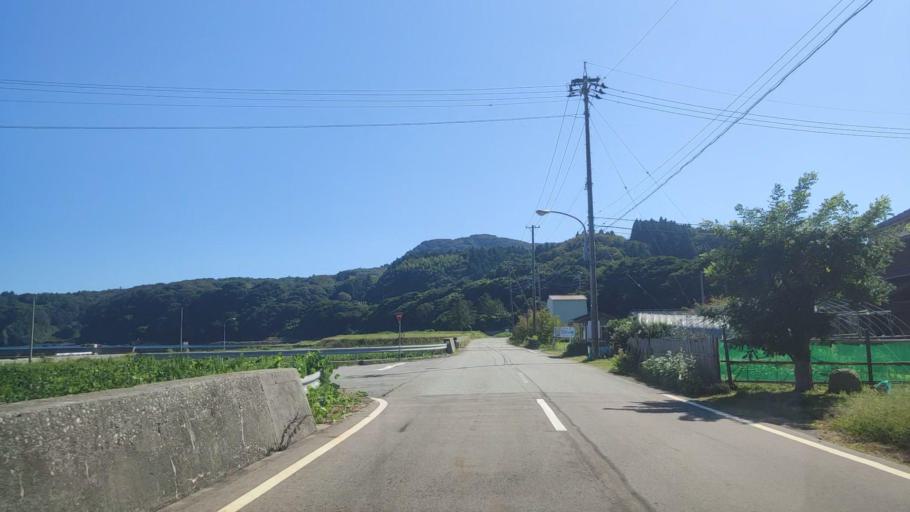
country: JP
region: Ishikawa
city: Nanao
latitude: 37.5233
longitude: 137.3262
